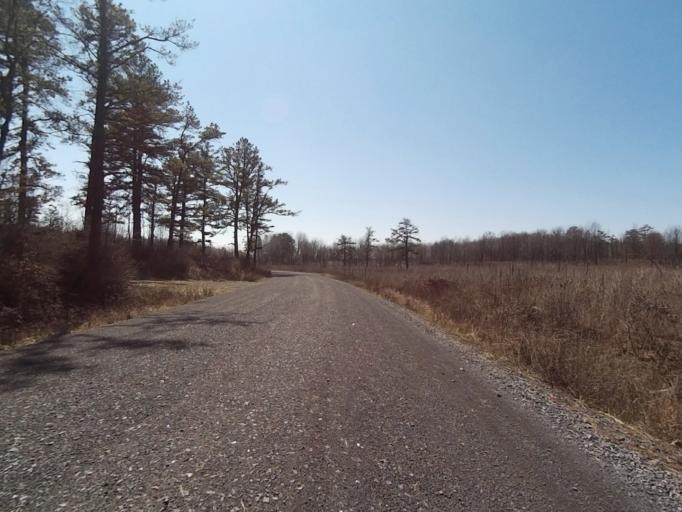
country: US
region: Pennsylvania
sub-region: Centre County
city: Park Forest Village
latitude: 40.7765
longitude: -77.9589
